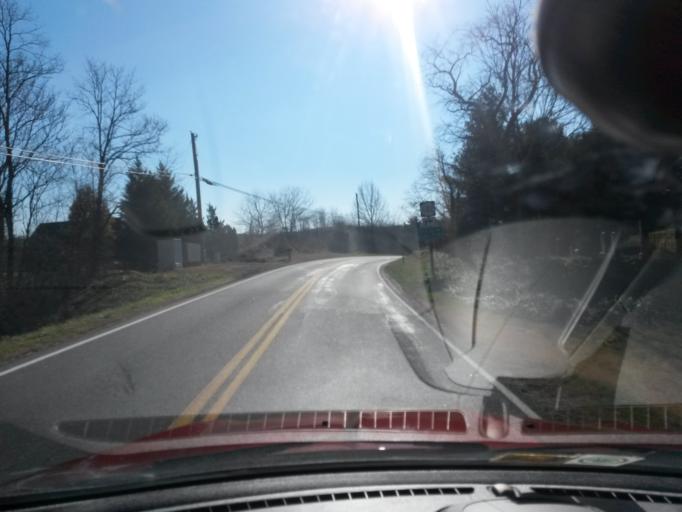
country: US
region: Virginia
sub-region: City of Bedford
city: Bedford
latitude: 37.3990
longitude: -79.5555
